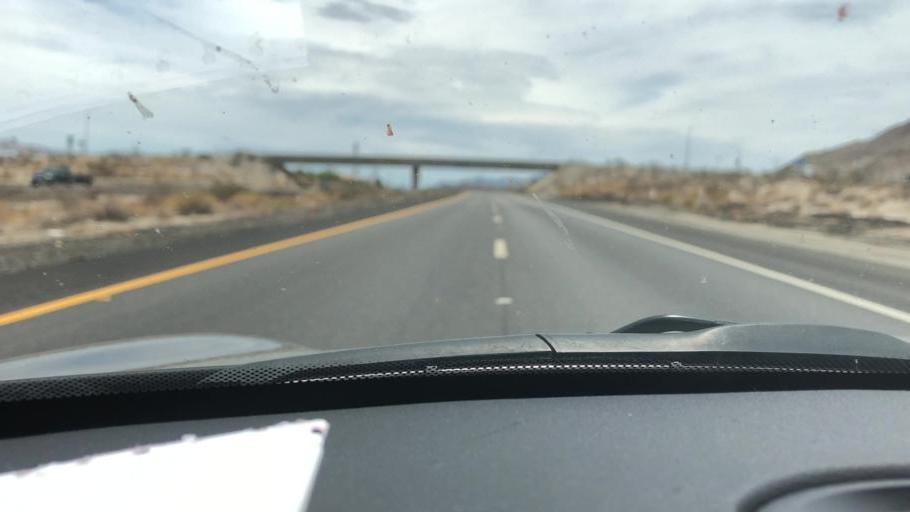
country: US
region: California
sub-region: Riverside County
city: Mecca
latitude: 33.6598
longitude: -115.7261
